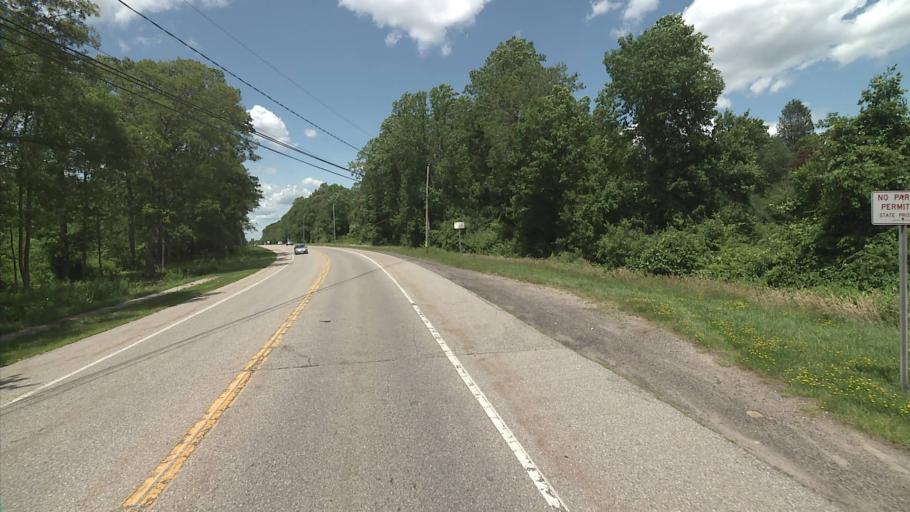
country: US
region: Connecticut
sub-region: New London County
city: Mystic
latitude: 41.3571
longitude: -71.9779
